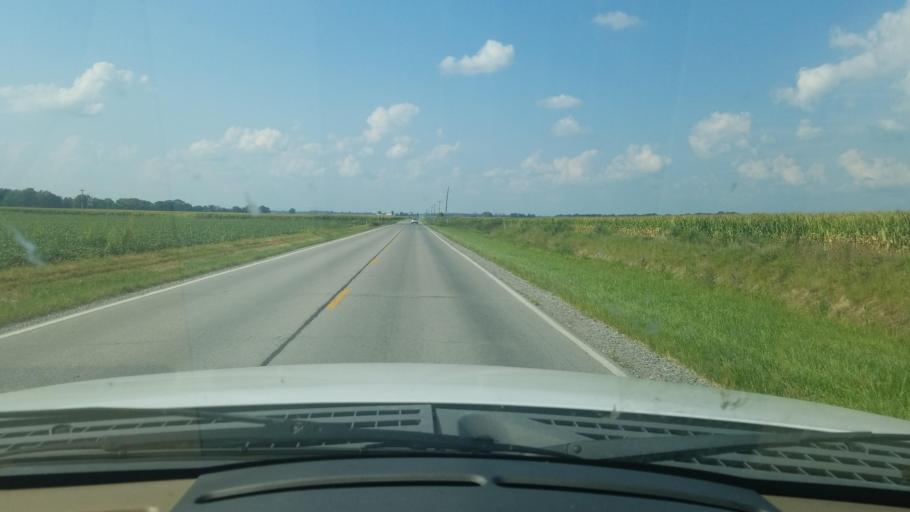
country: US
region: Illinois
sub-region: Saline County
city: Eldorado
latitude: 37.8359
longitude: -88.4526
